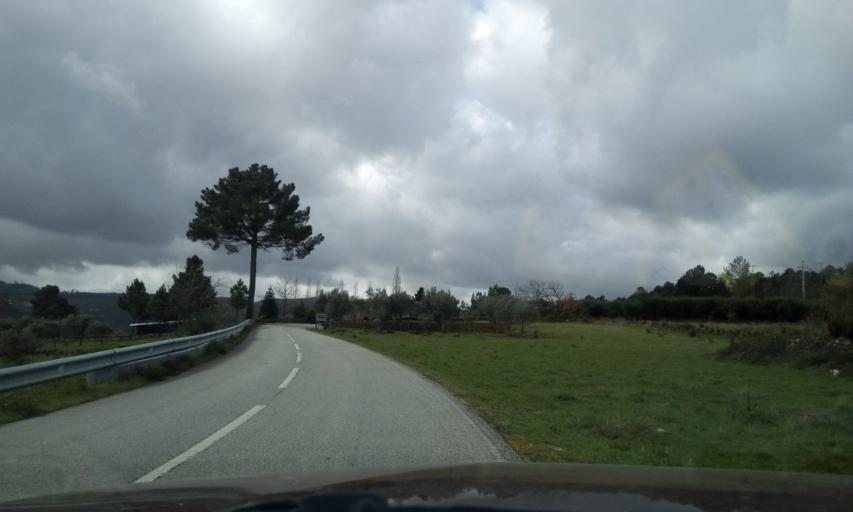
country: PT
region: Guarda
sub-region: Fornos de Algodres
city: Fornos de Algodres
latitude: 40.6602
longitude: -7.5777
